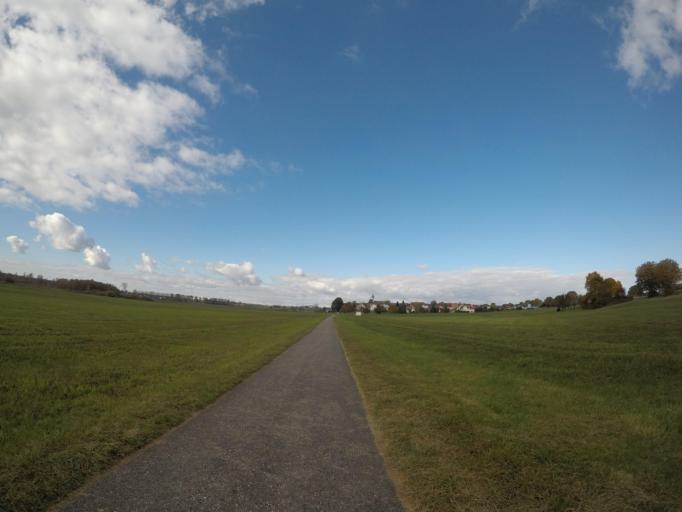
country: DE
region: Baden-Wuerttemberg
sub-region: Tuebingen Region
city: Seekirch
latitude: 48.1007
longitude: 9.6459
